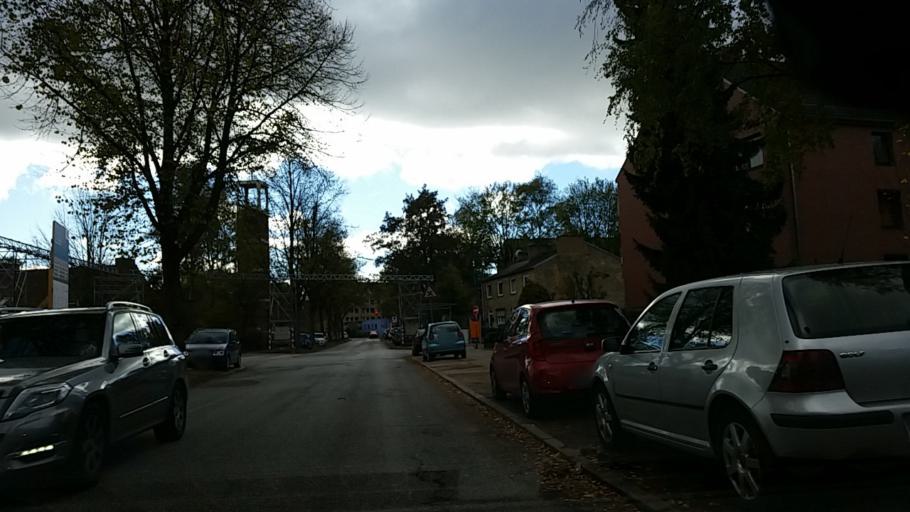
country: DE
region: Hamburg
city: Wandsbek
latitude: 53.5405
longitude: 10.1274
